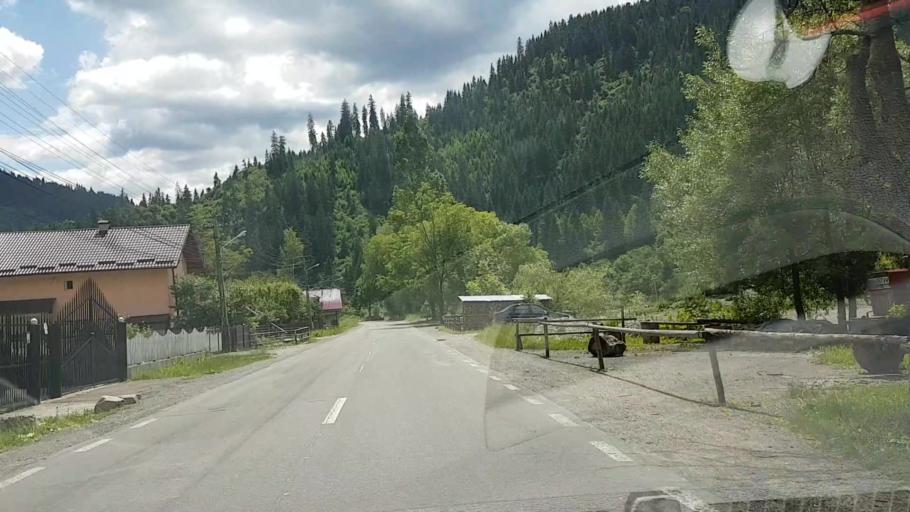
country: RO
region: Suceava
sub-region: Comuna Brosteni
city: Brosteni
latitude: 47.2416
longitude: 25.6910
